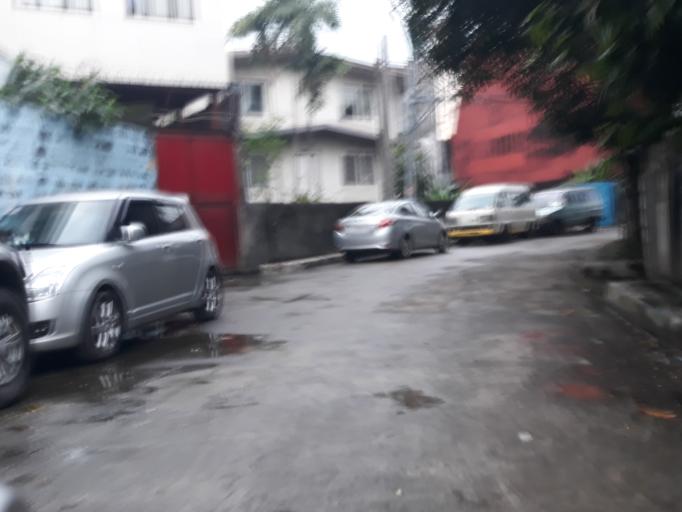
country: PH
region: Metro Manila
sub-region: San Juan
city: San Juan
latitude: 14.6117
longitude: 121.0239
